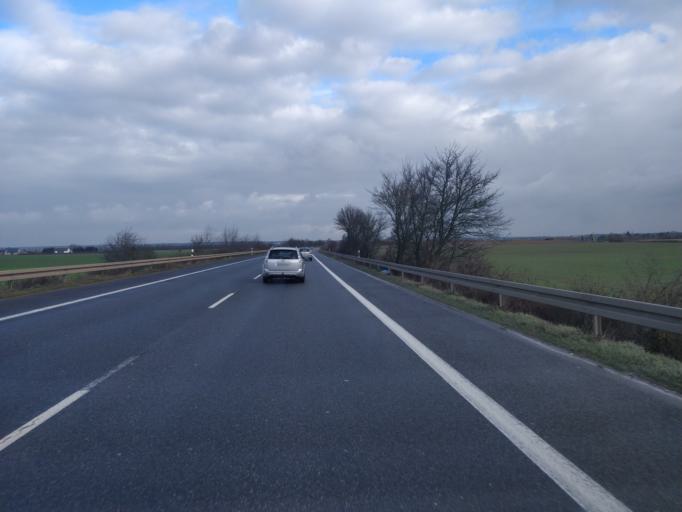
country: DE
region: North Rhine-Westphalia
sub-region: Regierungsbezirk Koln
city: Weilerswist
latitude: 50.6975
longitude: 6.8546
